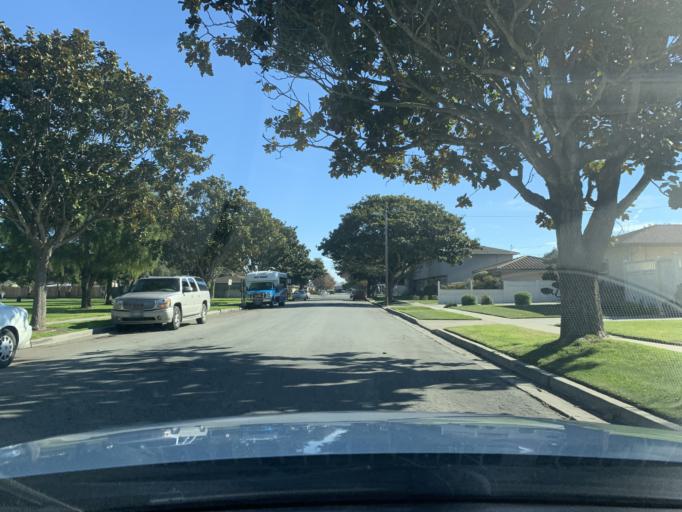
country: US
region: California
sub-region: Monterey County
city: Salinas
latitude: 36.6688
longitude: -121.6753
